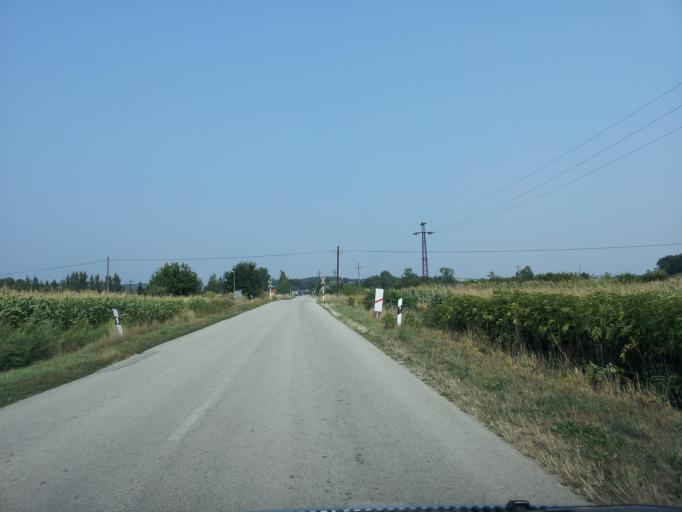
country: HU
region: Gyor-Moson-Sopron
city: Bakonyszentlaszlo
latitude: 47.4386
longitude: 17.7943
